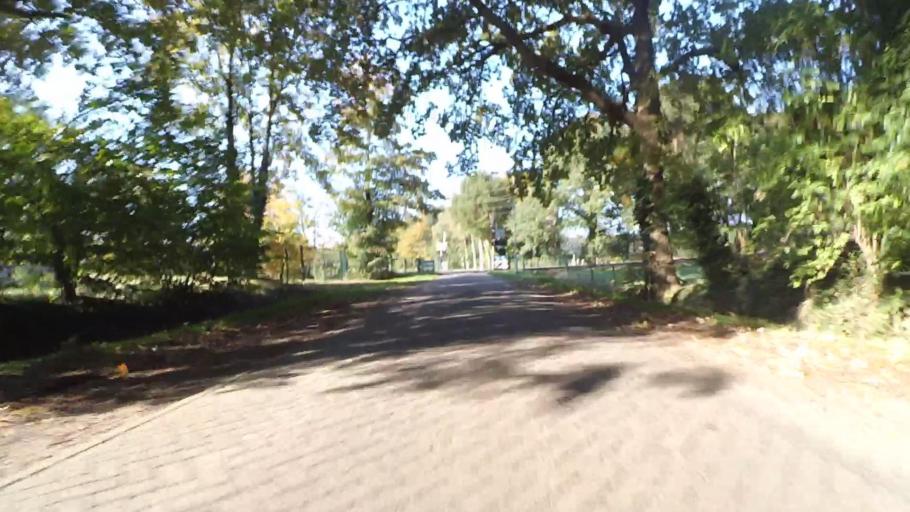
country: NL
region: Gelderland
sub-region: Gemeente Putten
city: Putten
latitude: 52.2715
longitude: 5.5848
